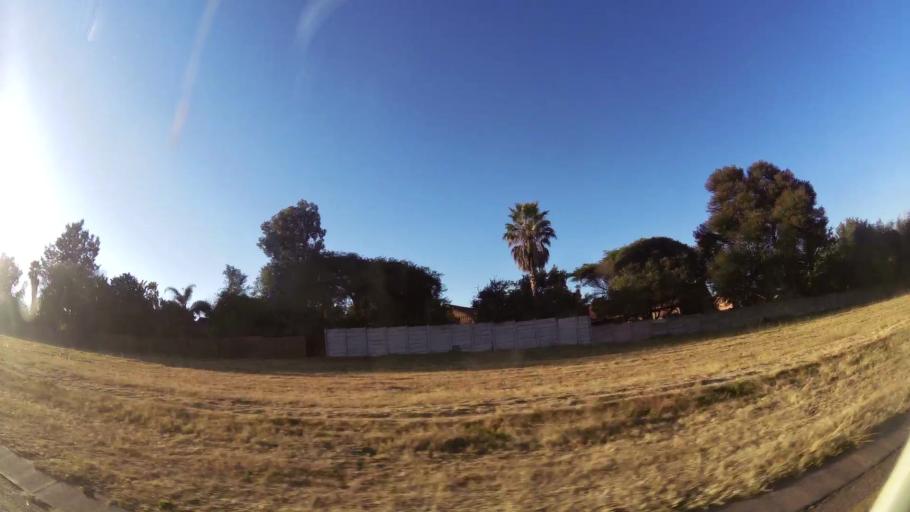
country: ZA
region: Gauteng
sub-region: City of Tshwane Metropolitan Municipality
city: Centurion
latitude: -25.8957
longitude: 28.1473
